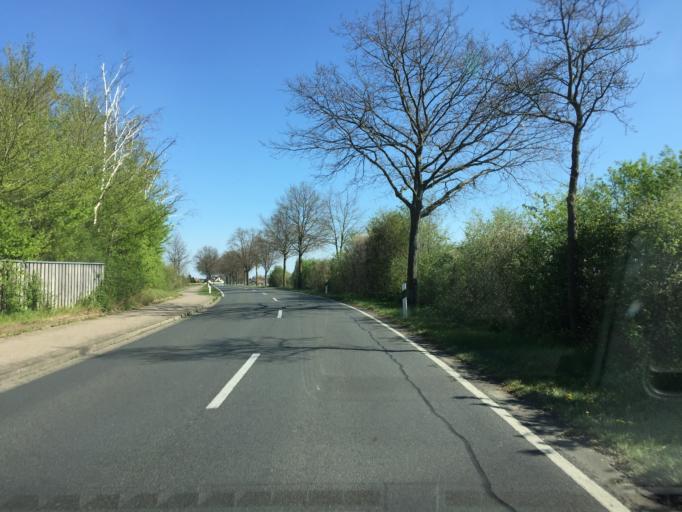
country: DE
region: Lower Saxony
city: Garbsen
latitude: 52.4044
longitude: 9.5415
